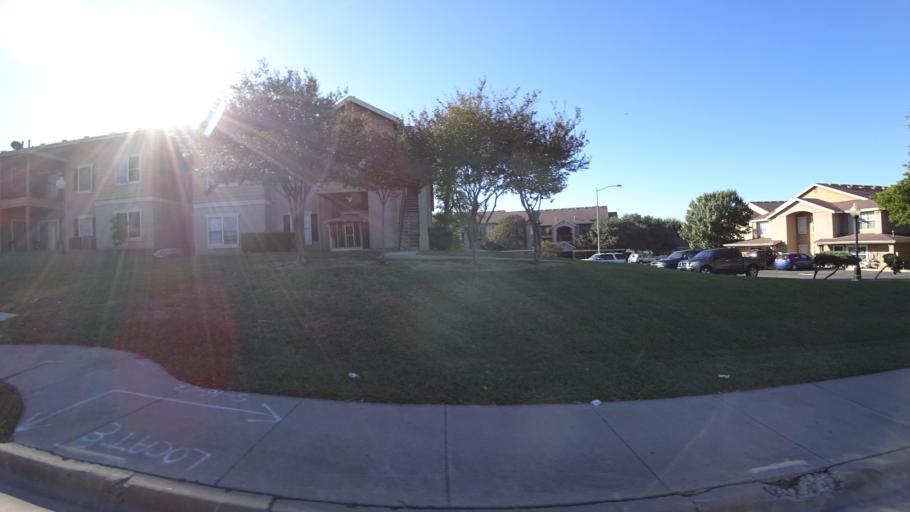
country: US
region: Texas
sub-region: Travis County
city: Austin
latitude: 30.2307
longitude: -97.7212
